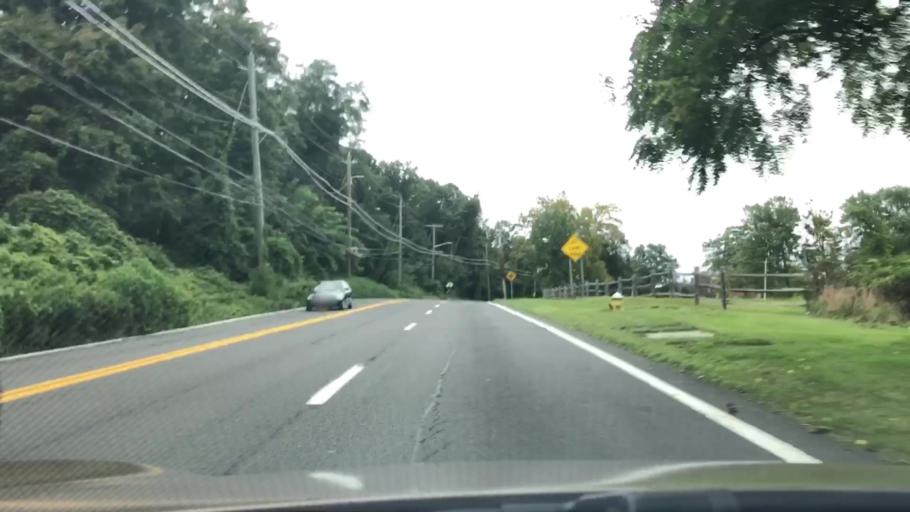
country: US
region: New York
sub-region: Westchester County
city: Sleepy Hollow
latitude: 41.1217
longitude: -73.8614
